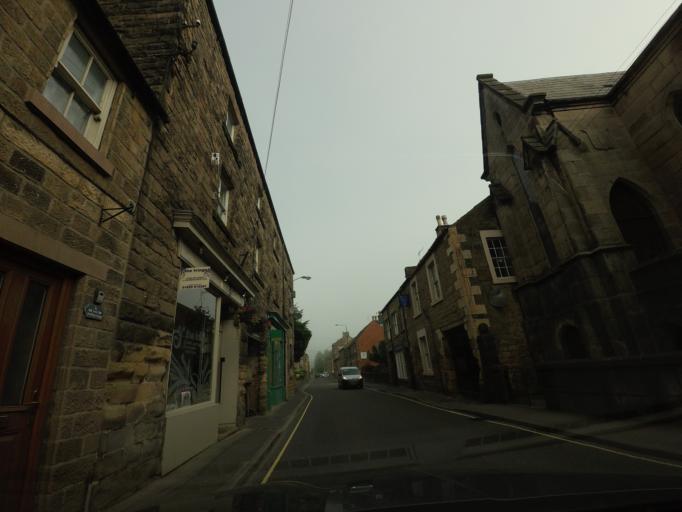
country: GB
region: England
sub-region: Derbyshire
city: Bakewell
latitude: 53.2145
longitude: -1.6768
